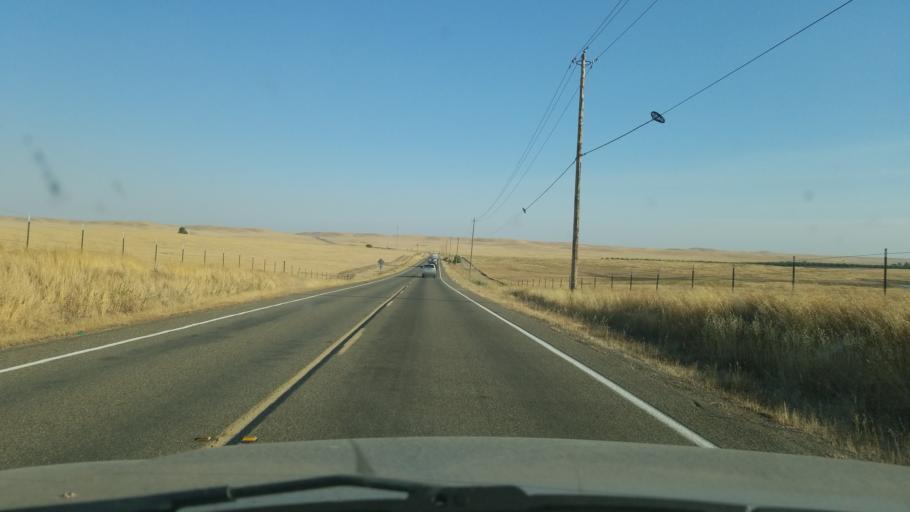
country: US
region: California
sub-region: Merced County
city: Merced
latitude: 37.4869
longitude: -120.4464
